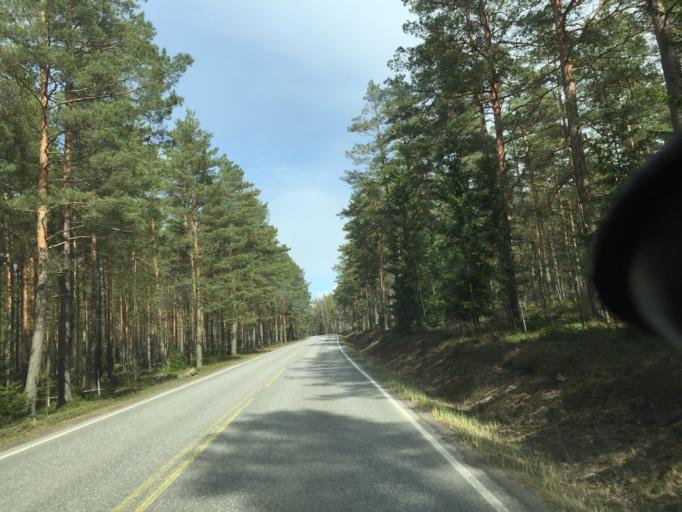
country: FI
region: Varsinais-Suomi
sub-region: Salo
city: Saerkisalo
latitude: 59.9767
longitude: 23.0063
